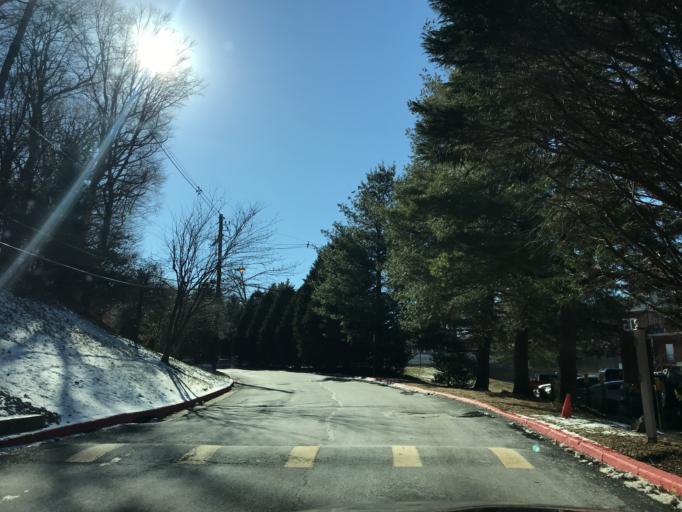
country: US
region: Maryland
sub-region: Baltimore County
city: Towson
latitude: 39.3737
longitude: -76.6341
